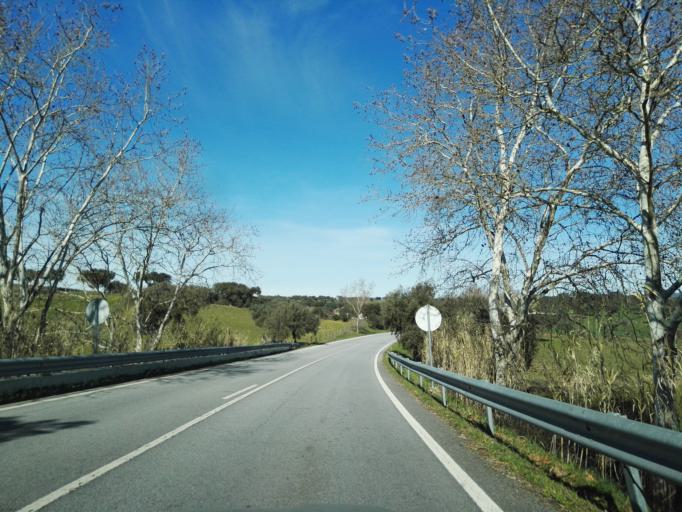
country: PT
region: Portalegre
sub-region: Arronches
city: Arronches
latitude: 39.0899
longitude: -7.2835
